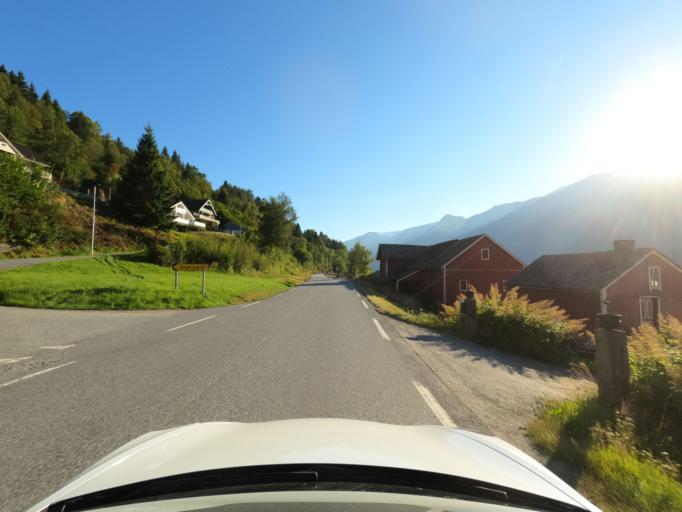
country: NO
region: Hordaland
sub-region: Odda
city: Odda
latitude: 60.2272
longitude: 6.6093
